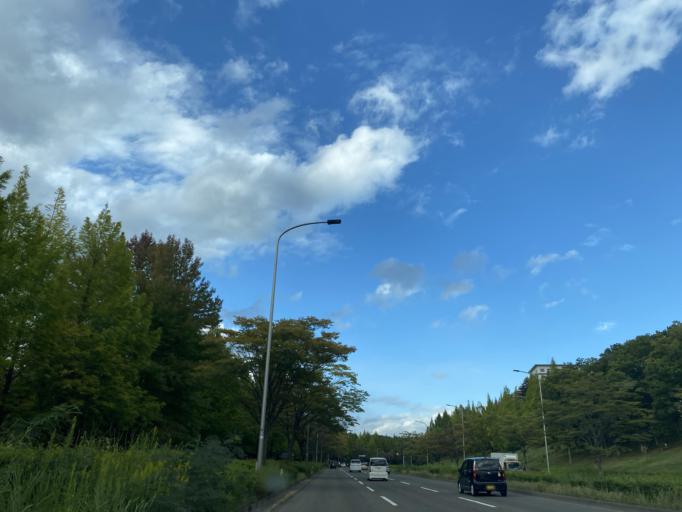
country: JP
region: Miyagi
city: Tomiya
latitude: 38.3380
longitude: 140.8392
